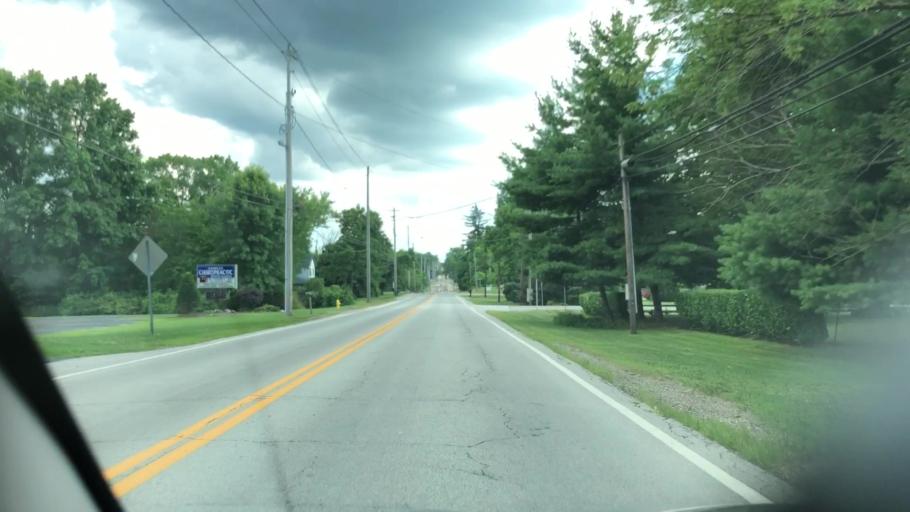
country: US
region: Ohio
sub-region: Summit County
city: Fairlawn
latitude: 41.1083
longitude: -81.6446
